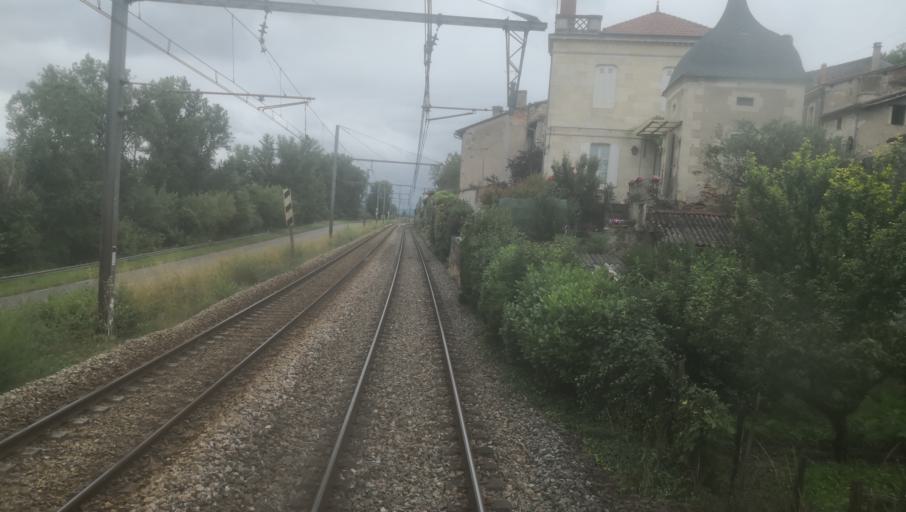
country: FR
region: Aquitaine
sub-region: Departement du Lot-et-Garonne
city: Port-Sainte-Marie
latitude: 44.2504
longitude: 0.4027
